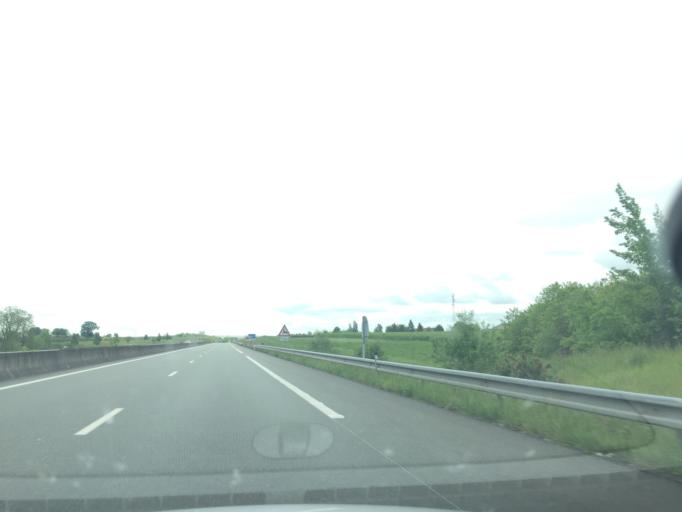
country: FR
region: Pays de la Loire
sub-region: Departement de la Sarthe
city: Luceau
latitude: 47.6881
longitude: 0.3647
